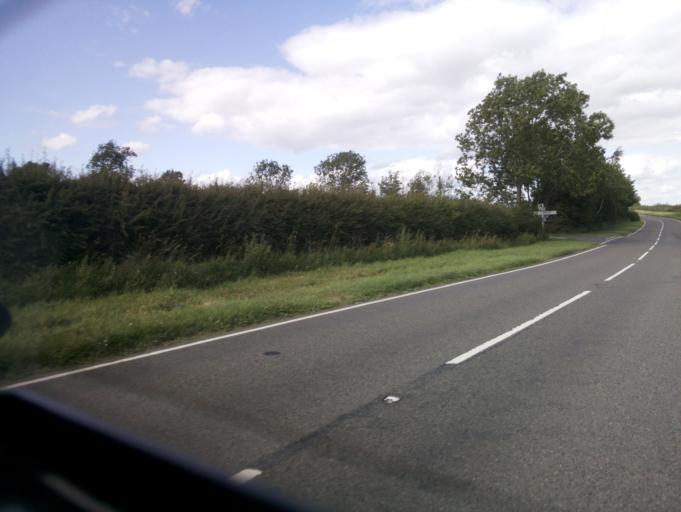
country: GB
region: England
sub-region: Leicestershire
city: Coalville
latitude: 52.7744
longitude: -1.3668
